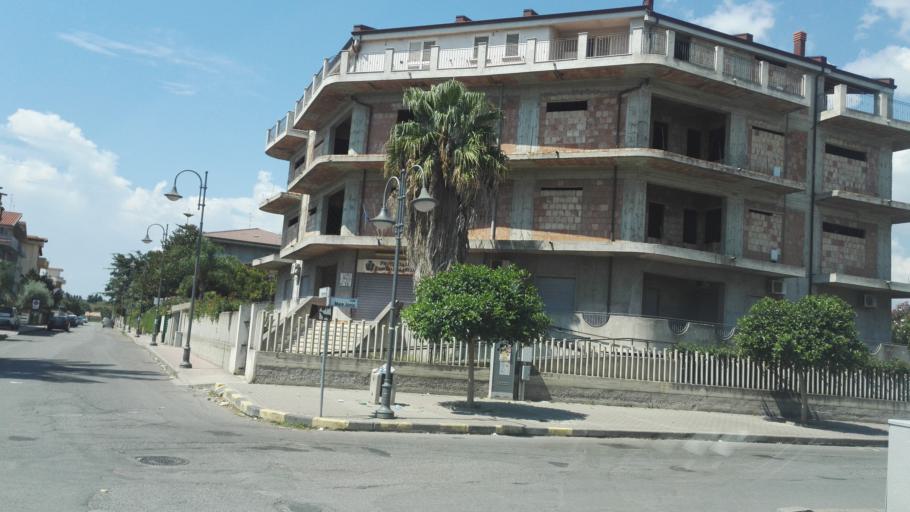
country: IT
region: Calabria
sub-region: Provincia di Reggio Calabria
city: Caulonia Marina
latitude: 38.3426
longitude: 16.4657
